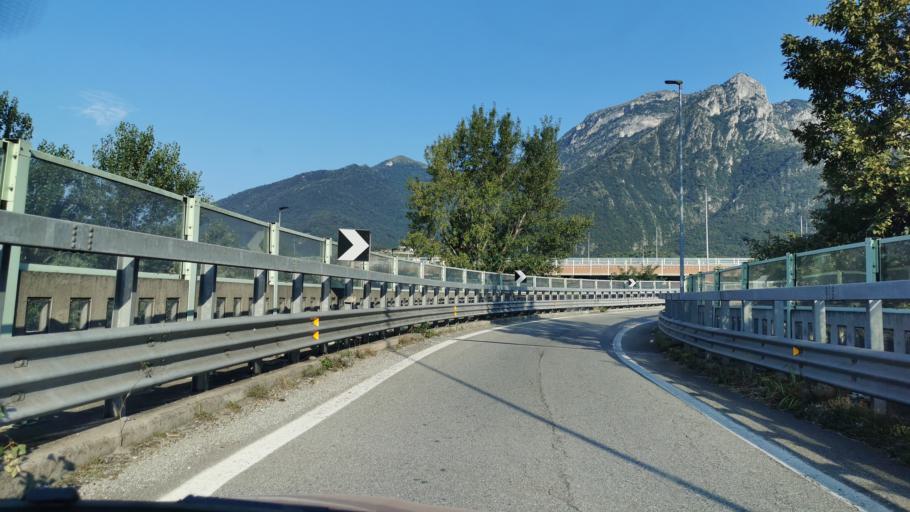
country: IT
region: Lombardy
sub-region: Provincia di Lecco
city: Civate
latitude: 45.8274
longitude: 9.3534
